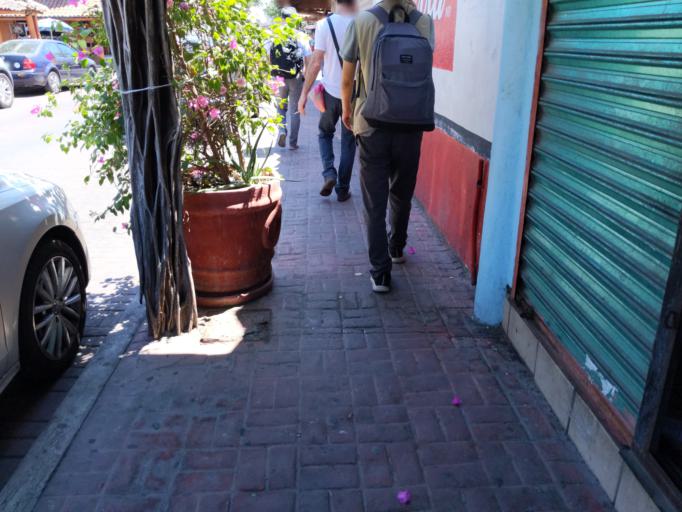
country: MX
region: Guerrero
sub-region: Zihuatanejo de Azueta
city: Ixtapa-Zihuatanejo
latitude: 17.6411
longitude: -101.5576
